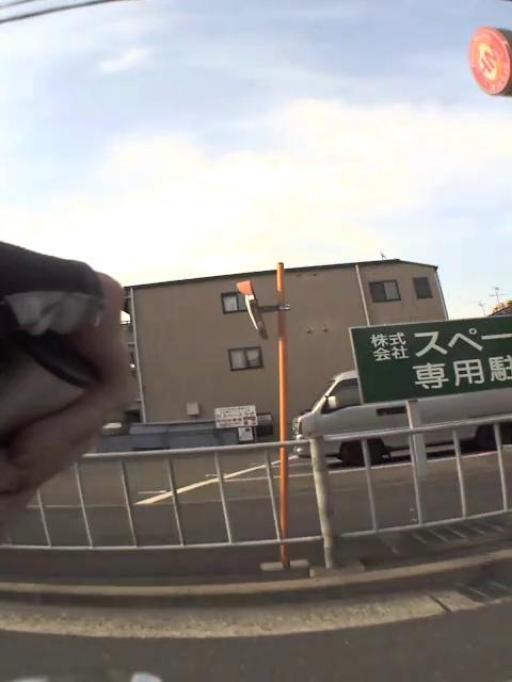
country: JP
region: Osaka
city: Kadoma
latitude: 34.7337
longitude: 135.5790
